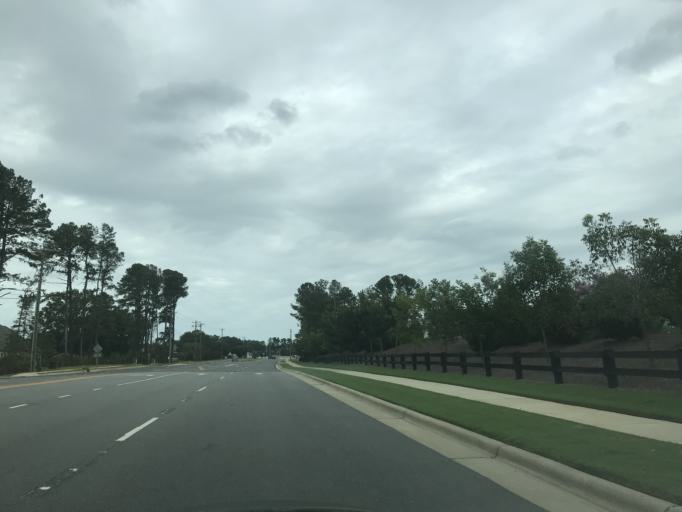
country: US
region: North Carolina
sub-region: Wake County
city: Cary
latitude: 35.7393
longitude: -78.7432
